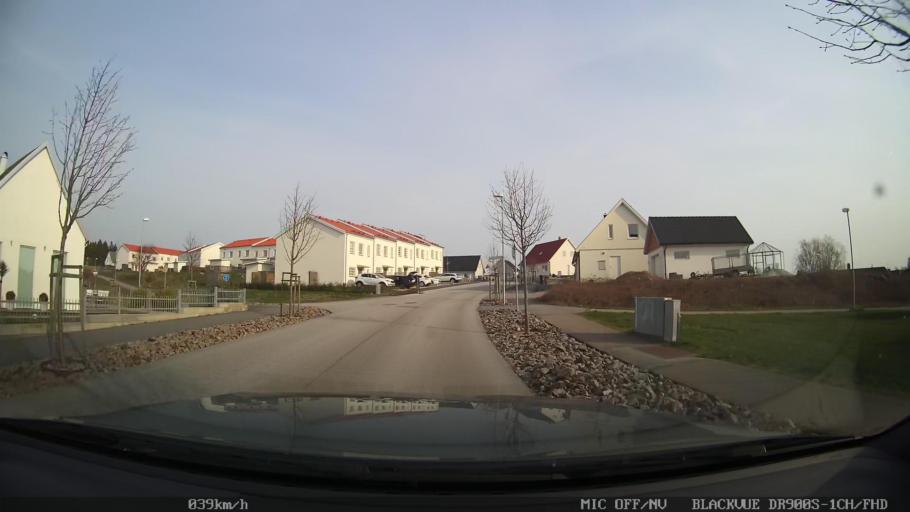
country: SE
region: Skane
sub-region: Ystads Kommun
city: Ystad
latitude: 55.4437
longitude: 13.7968
